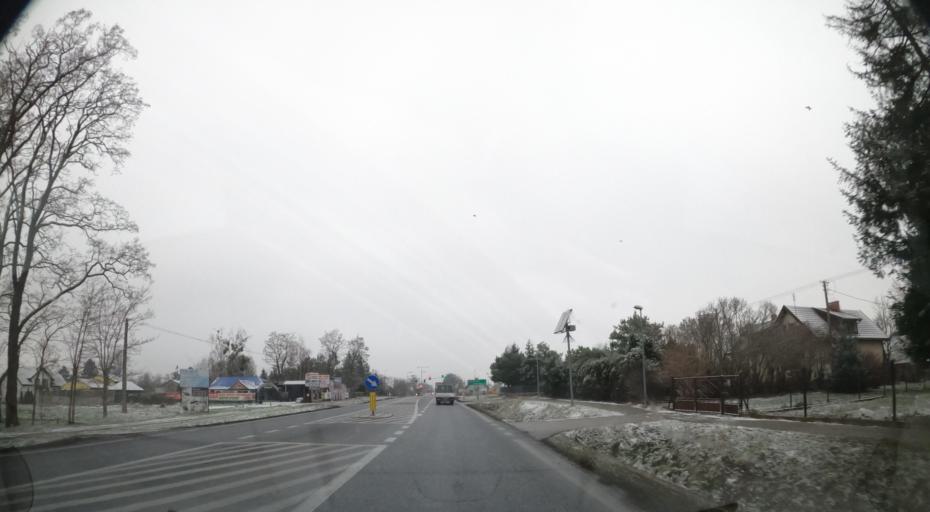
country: PL
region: Masovian Voivodeship
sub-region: Powiat sochaczewski
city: Paprotnia
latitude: 52.2130
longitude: 20.4183
